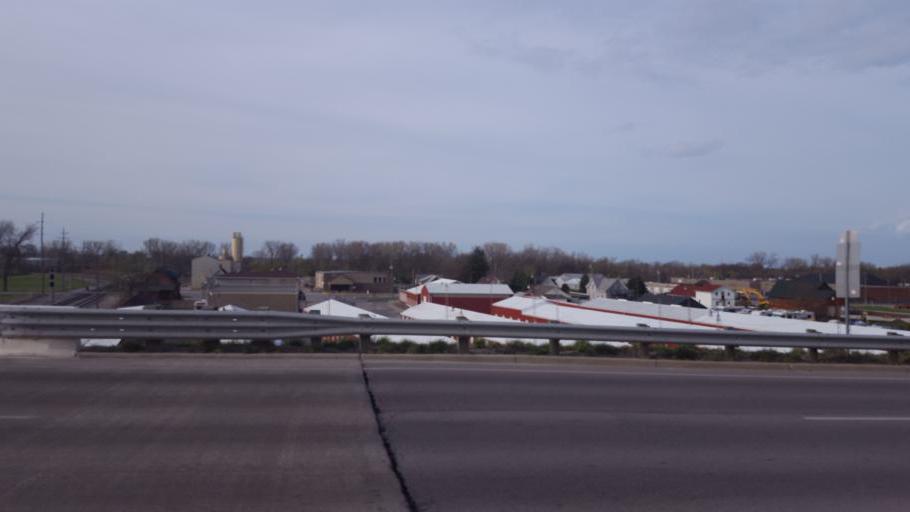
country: US
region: Ohio
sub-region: Erie County
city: Sandusky
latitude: 41.4388
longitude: -82.7402
